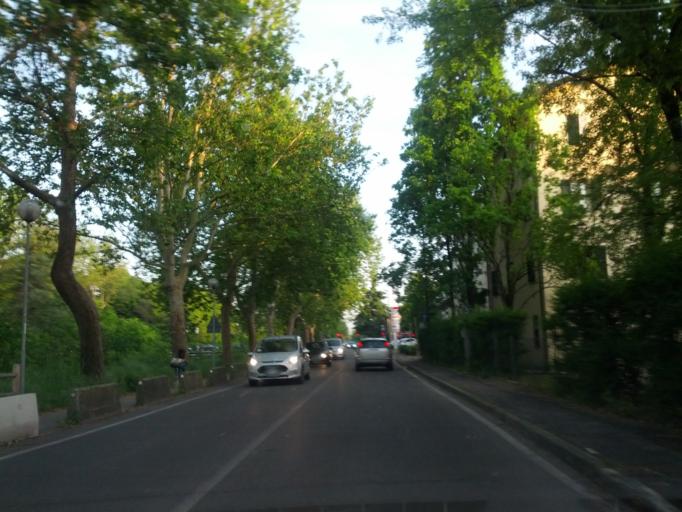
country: IT
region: Emilia-Romagna
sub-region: Provincia di Reggio Emilia
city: Reggio nell'Emilia
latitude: 44.6993
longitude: 10.6178
